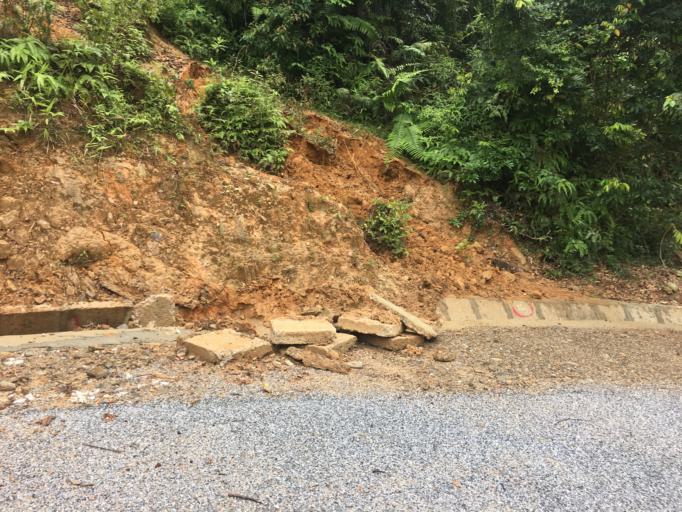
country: VN
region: Ha Giang
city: Thi Tran Tam Son
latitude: 22.9935
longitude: 105.0689
